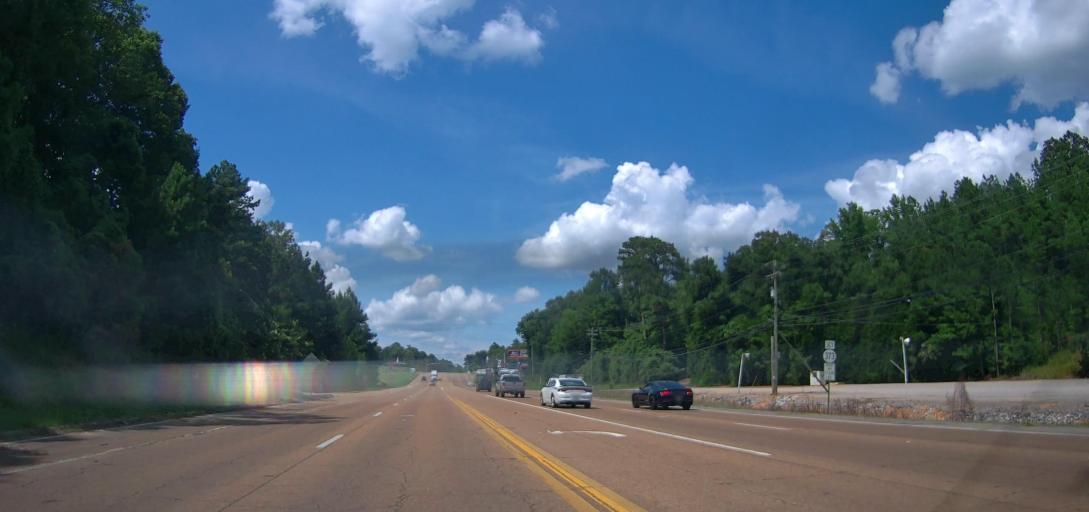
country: US
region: Mississippi
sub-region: Lowndes County
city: Columbus
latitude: 33.5587
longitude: -88.4330
